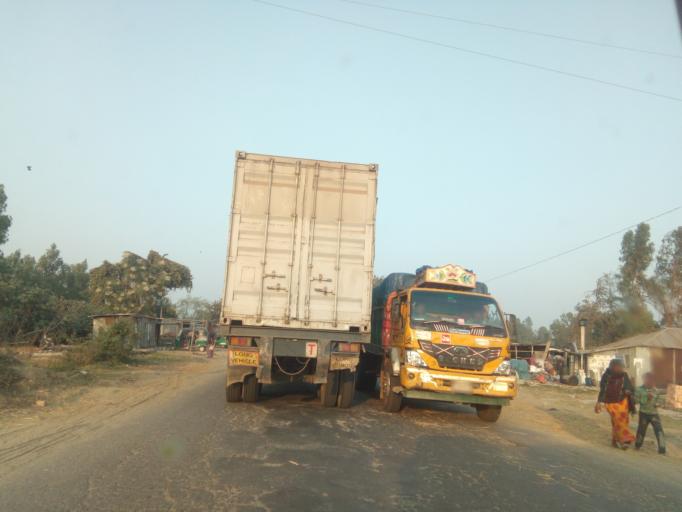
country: BD
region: Rajshahi
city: Bogra
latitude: 24.5549
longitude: 89.1957
